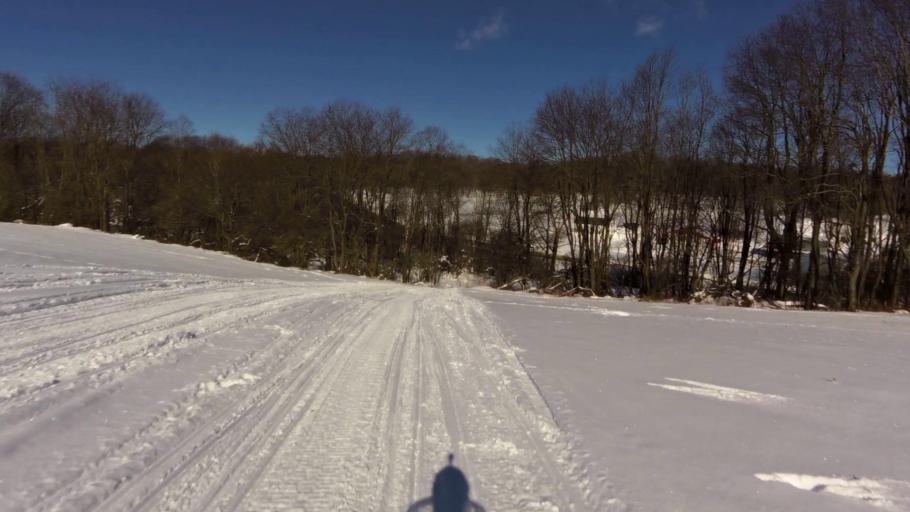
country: US
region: New York
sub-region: Cattaraugus County
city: Franklinville
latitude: 42.3913
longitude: -78.4853
